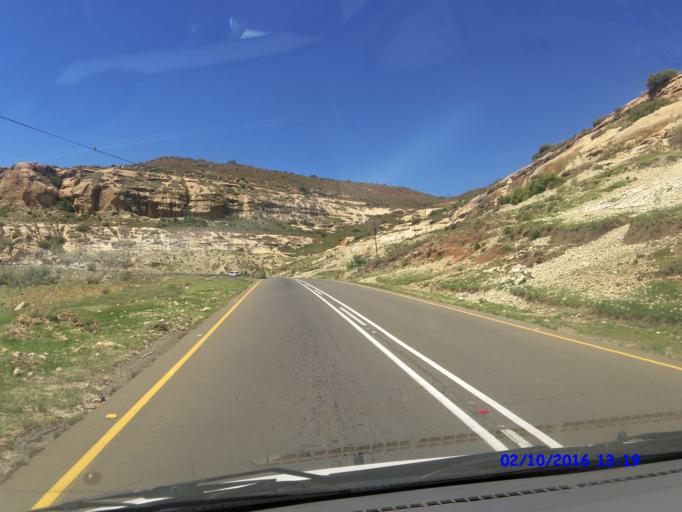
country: LS
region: Maseru
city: Nako
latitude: -29.4237
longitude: 27.6961
